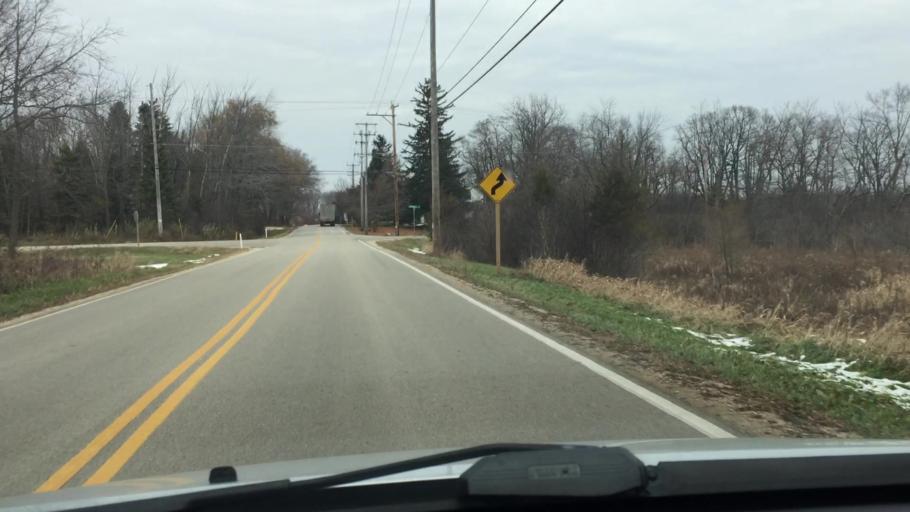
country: US
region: Wisconsin
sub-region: Ozaukee County
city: Thiensville
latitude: 43.2645
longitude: -87.9757
